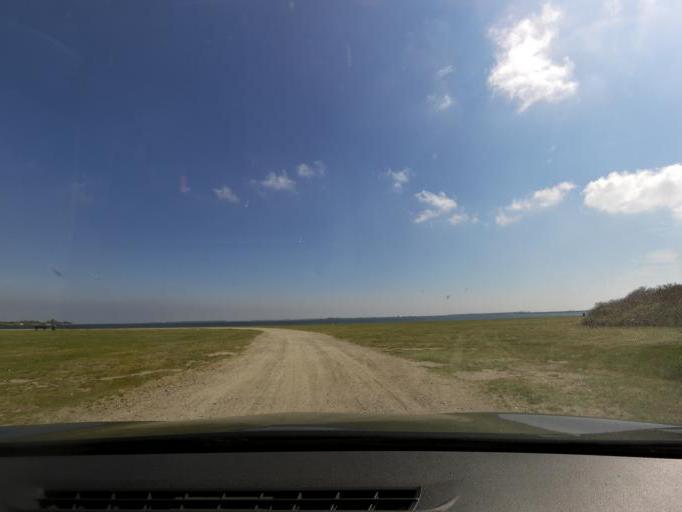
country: NL
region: South Holland
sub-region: Gemeente Hellevoetsluis
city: Nieuw-Helvoet
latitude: 51.8405
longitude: 4.0632
